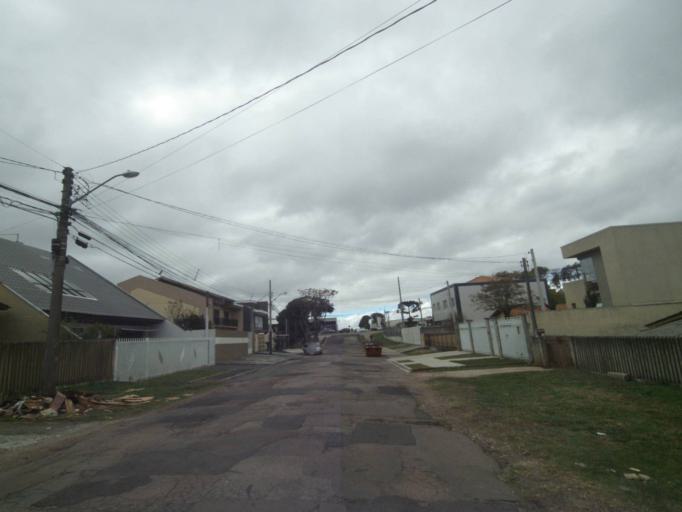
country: BR
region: Parana
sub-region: Sao Jose Dos Pinhais
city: Sao Jose dos Pinhais
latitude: -25.5396
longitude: -49.2957
